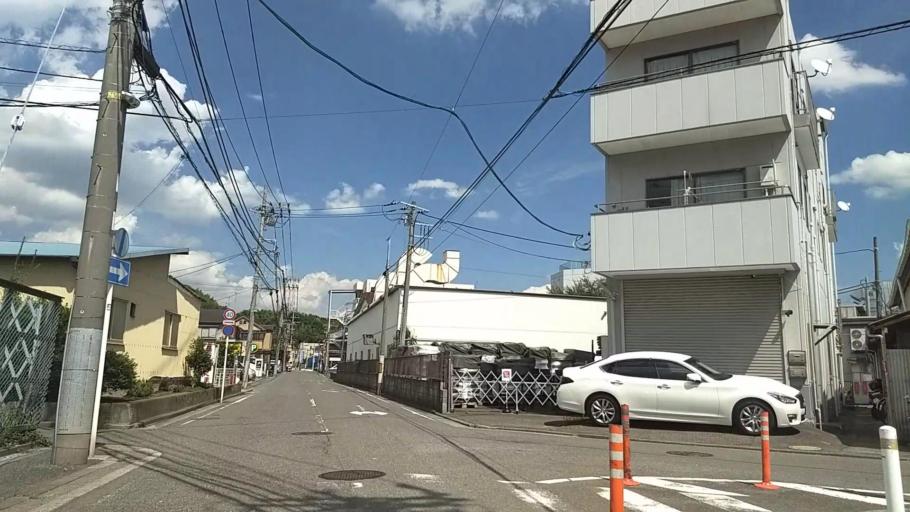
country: JP
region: Kanagawa
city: Yokohama
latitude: 35.5204
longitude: 139.5839
